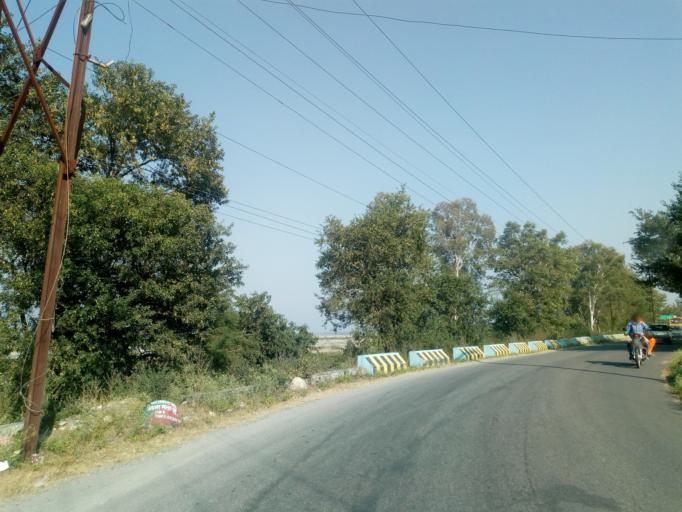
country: IN
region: Himachal Pradesh
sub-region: Sirmaur
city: Paonta Sahib
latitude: 30.4422
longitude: 77.6739
